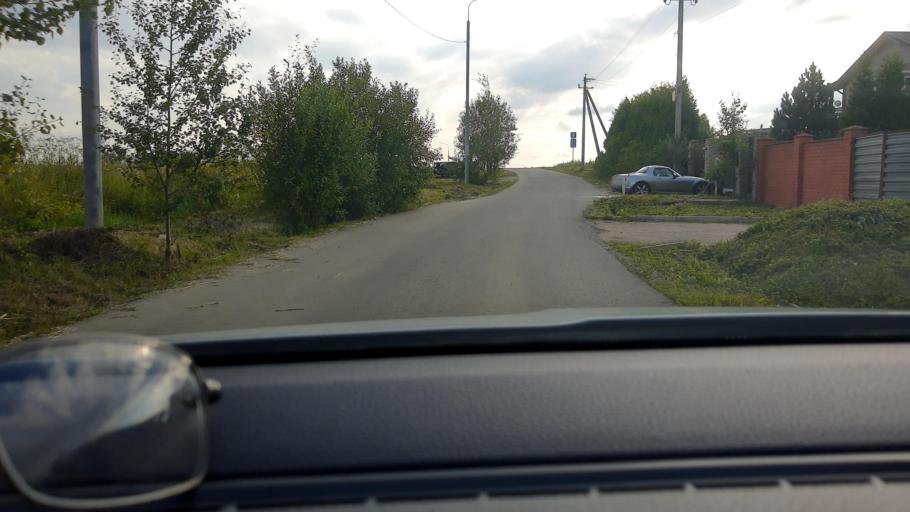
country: RU
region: Moskovskaya
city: Kokoshkino
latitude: 55.5895
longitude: 37.1614
